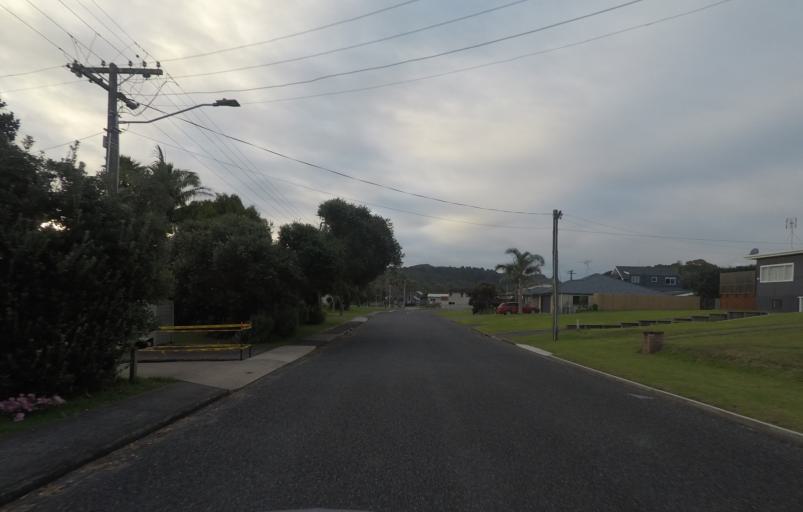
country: NZ
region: Bay of Plenty
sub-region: Western Bay of Plenty District
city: Waihi Beach
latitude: -37.4065
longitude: 175.9406
